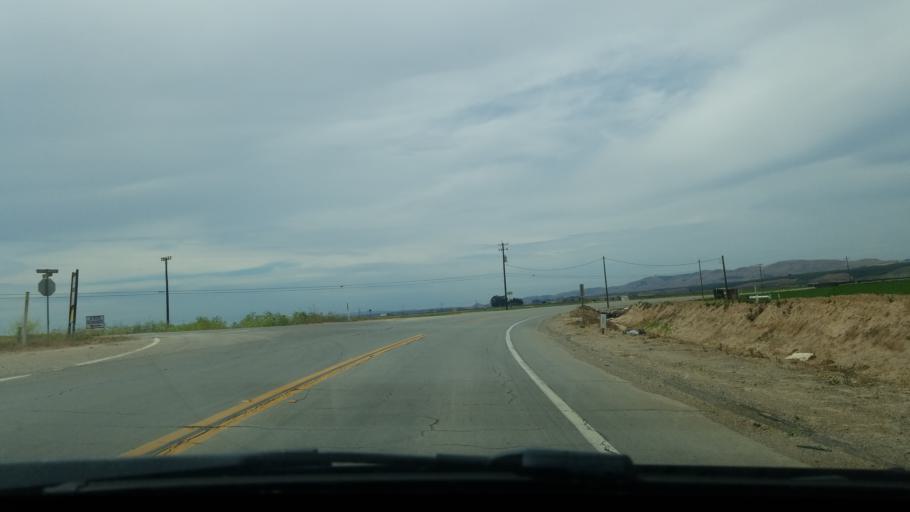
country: US
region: California
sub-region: Santa Barbara County
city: Santa Maria
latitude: 34.9100
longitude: -120.3468
